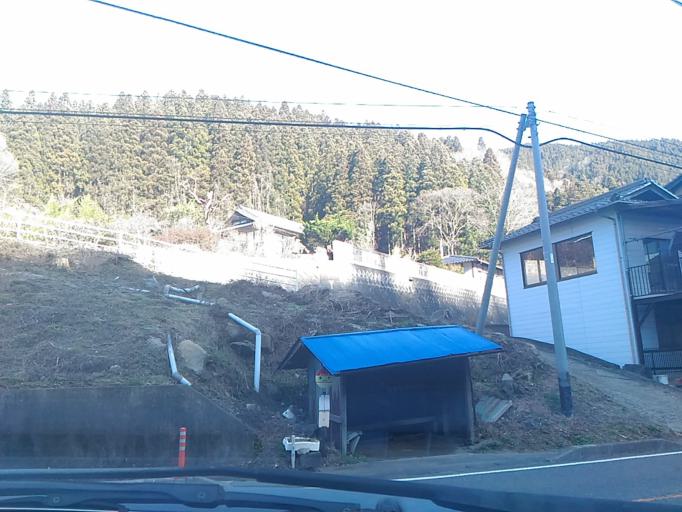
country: JP
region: Fukushima
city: Ishikawa
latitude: 37.0529
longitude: 140.6080
